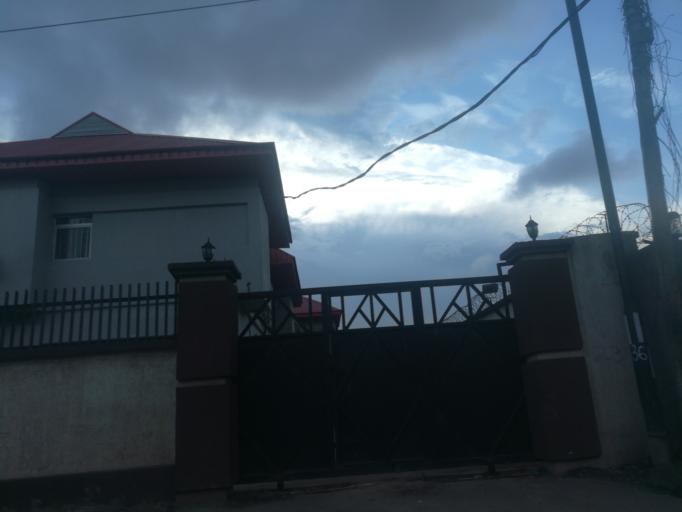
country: NG
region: Lagos
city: Ojota
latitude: 6.5661
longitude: 3.3687
